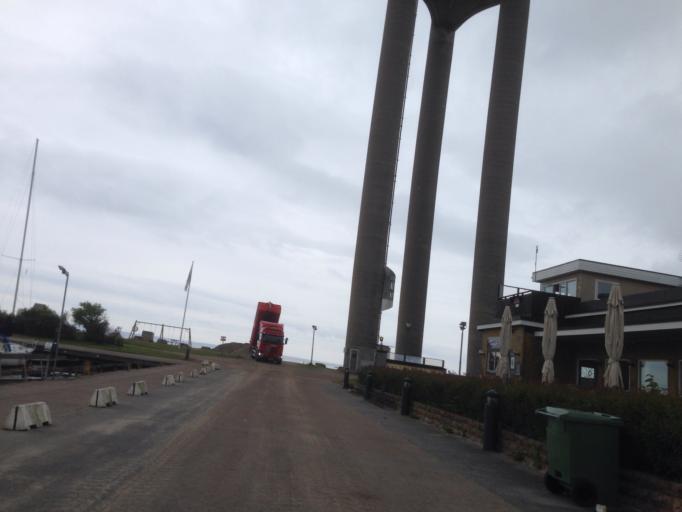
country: SE
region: Skane
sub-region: Landskrona
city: Landskrona
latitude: 55.8686
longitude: 12.8199
